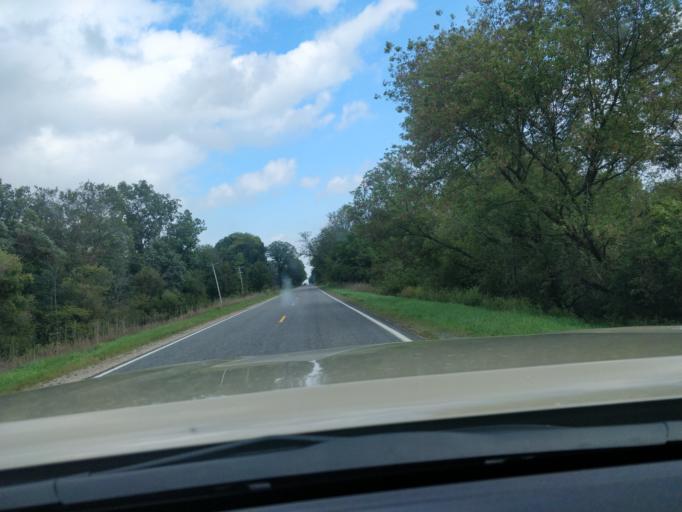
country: US
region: Michigan
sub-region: Ionia County
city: Saranac
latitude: 42.8862
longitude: -85.2527
